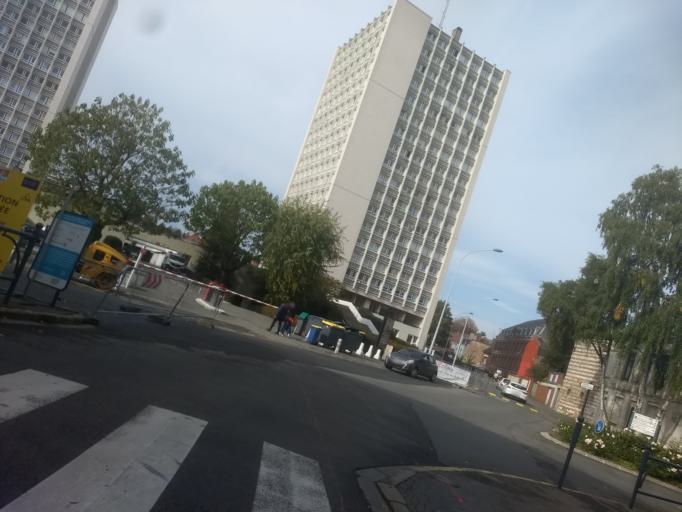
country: FR
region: Nord-Pas-de-Calais
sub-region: Departement du Pas-de-Calais
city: Arras
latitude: 50.2923
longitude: 2.7720
